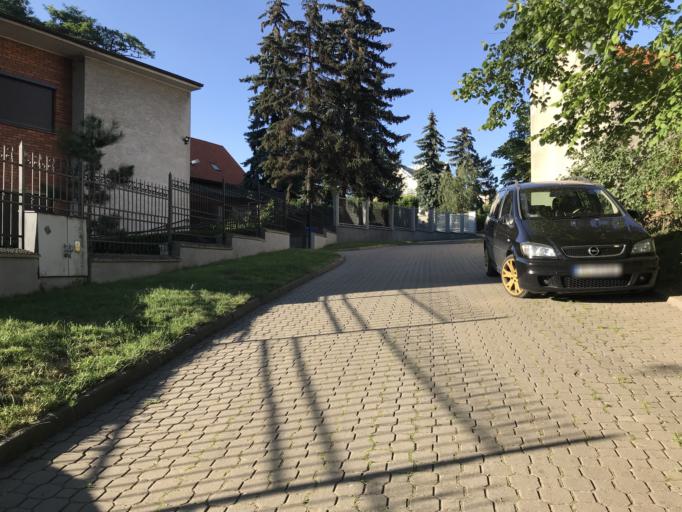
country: PL
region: Greater Poland Voivodeship
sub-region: Kalisz
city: Kalisz
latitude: 51.7665
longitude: 18.0998
